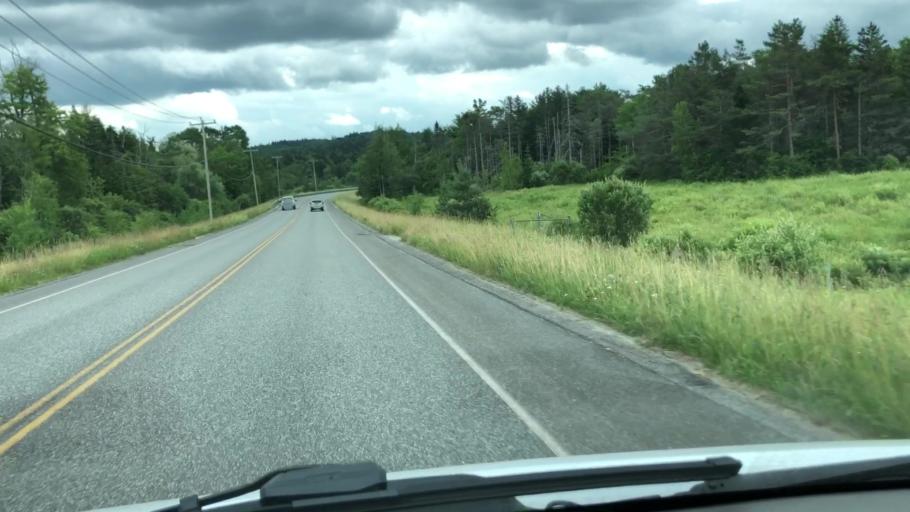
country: US
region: Massachusetts
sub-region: Berkshire County
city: Adams
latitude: 42.5331
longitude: -73.0572
